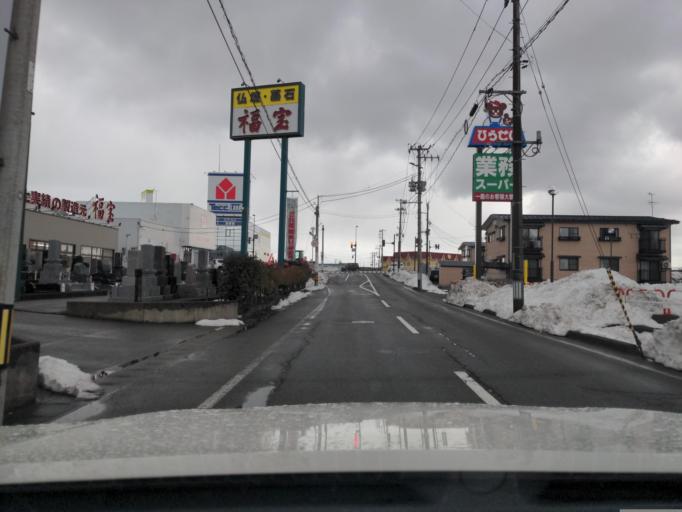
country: JP
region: Niigata
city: Kashiwazaki
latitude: 37.3614
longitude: 138.5681
